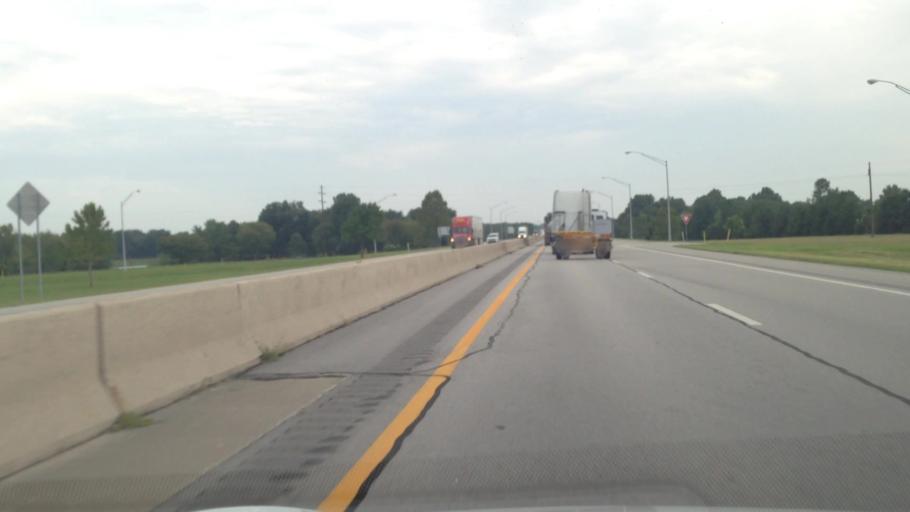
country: US
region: Oklahoma
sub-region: Ottawa County
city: Miami
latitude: 36.8642
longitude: -94.8505
